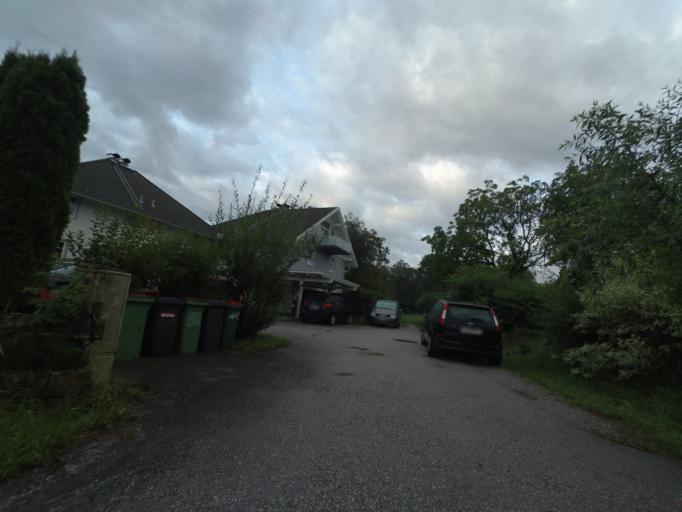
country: AT
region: Salzburg
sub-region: Politischer Bezirk Hallein
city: Puch bei Hallein
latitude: 47.7239
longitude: 13.0742
